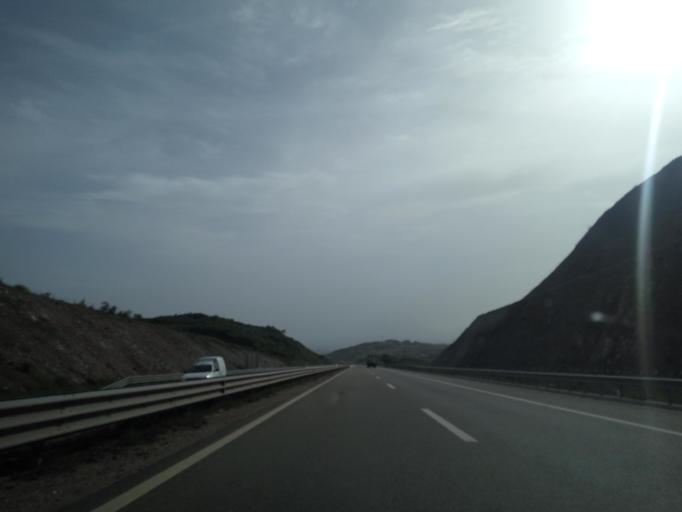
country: XK
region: Prizren
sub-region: Komuna e Therandes
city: Peqan
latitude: 42.3915
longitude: 20.8560
